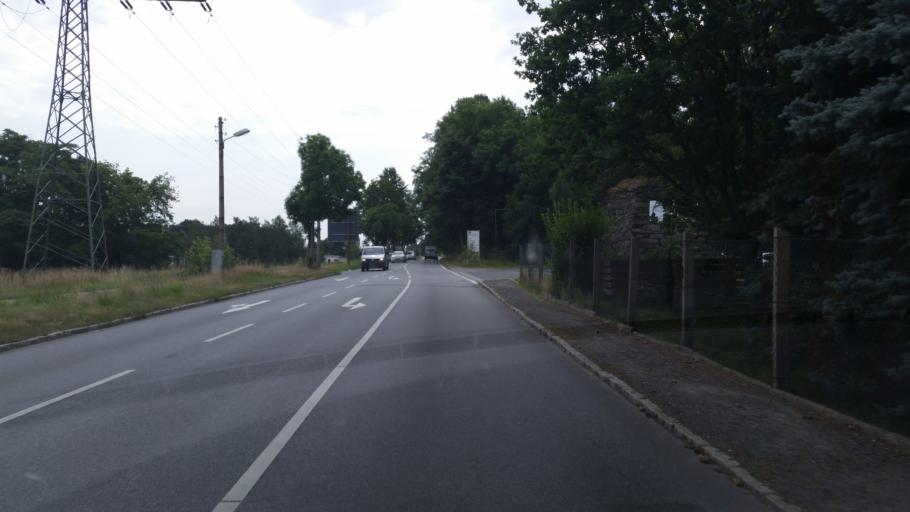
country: DE
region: Saxony
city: Kamenz
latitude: 51.2631
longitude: 14.1151
